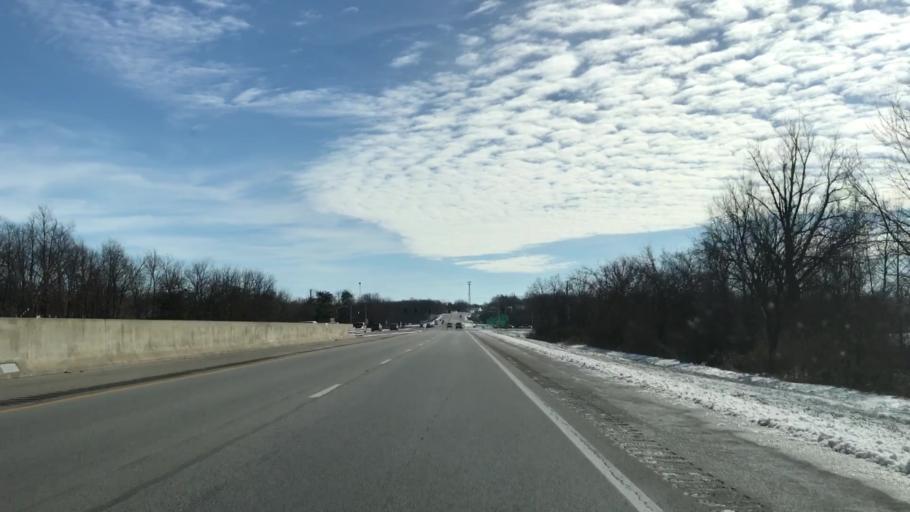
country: US
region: Kentucky
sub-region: Hardin County
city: Elizabethtown
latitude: 37.6937
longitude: -85.8747
